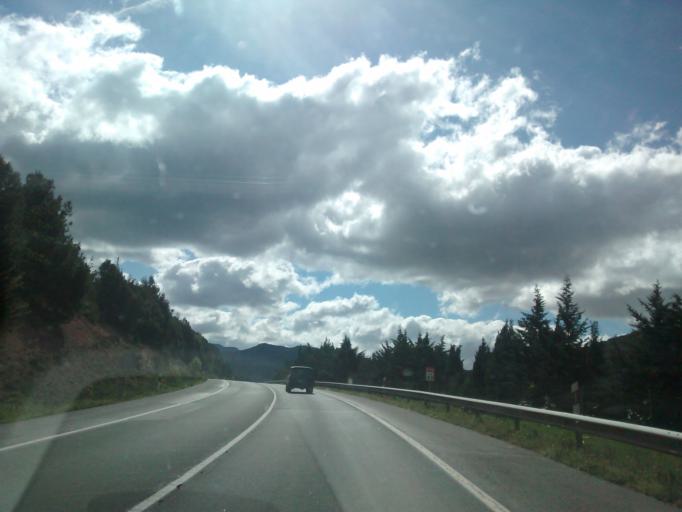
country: ES
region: Basque Country
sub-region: Provincia de Alava
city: Zambrana
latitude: 42.6427
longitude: -2.8678
